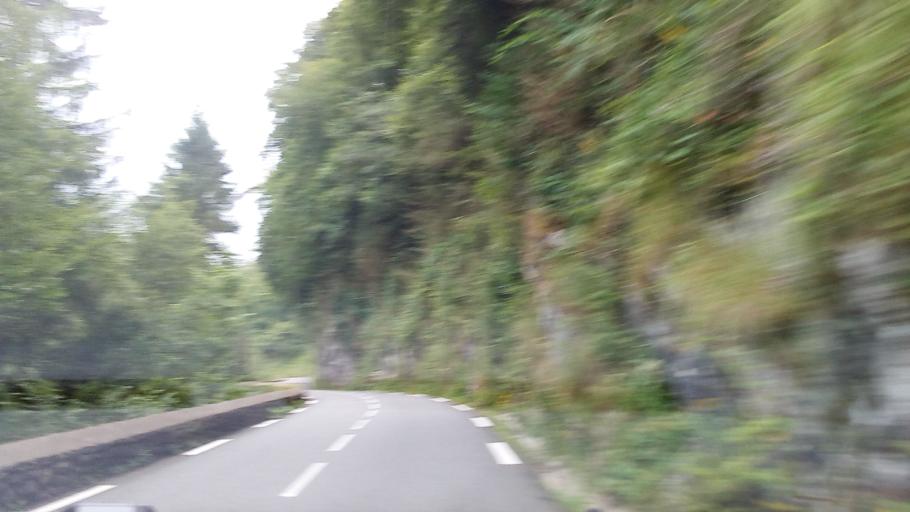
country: FR
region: Aquitaine
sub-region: Departement des Pyrenees-Atlantiques
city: Laruns
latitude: 42.9724
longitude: -0.3886
